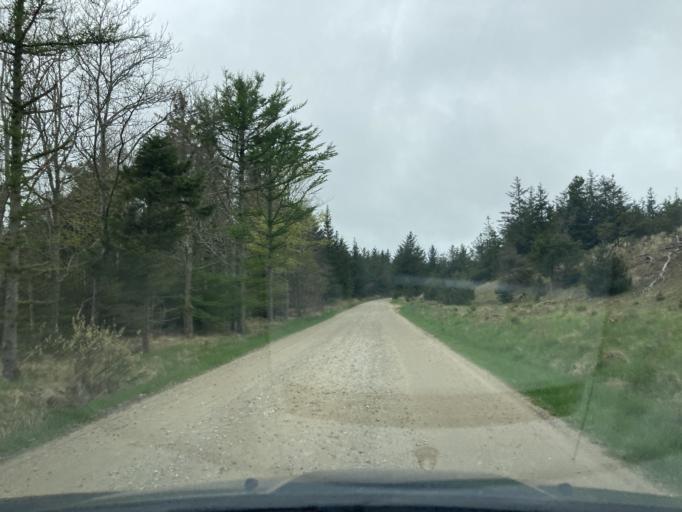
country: DK
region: Central Jutland
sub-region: Lemvig Kommune
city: Thyboron
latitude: 56.8160
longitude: 8.2796
